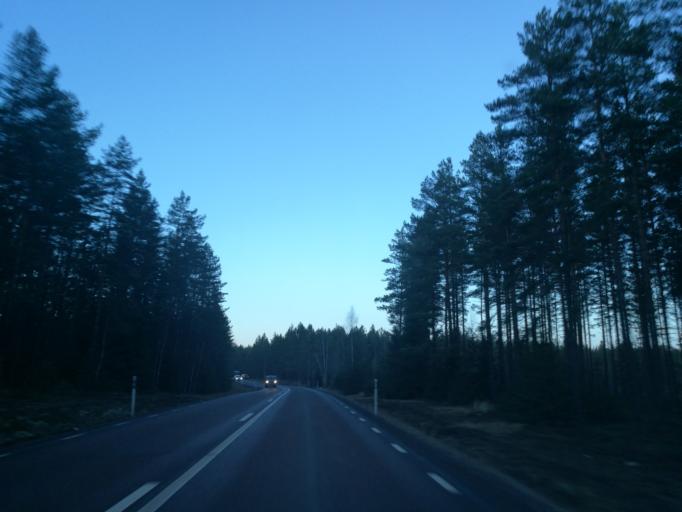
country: SE
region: Vaermland
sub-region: Eda Kommun
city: Charlottenberg
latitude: 59.9008
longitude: 12.2795
